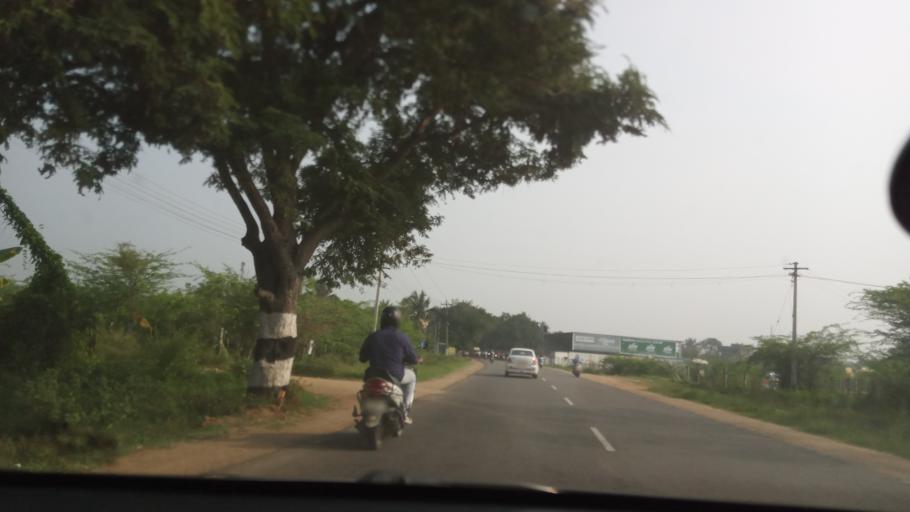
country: IN
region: Tamil Nadu
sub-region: Coimbatore
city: Periyanayakkanpalaiyam
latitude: 11.1472
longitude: 77.0441
